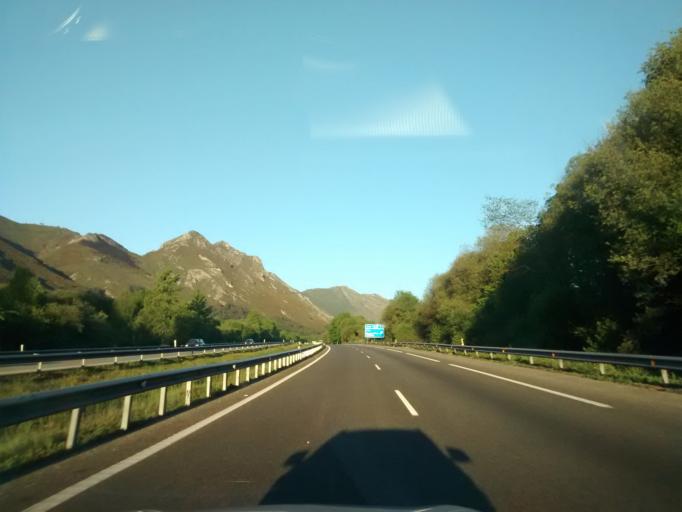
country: ES
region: Asturias
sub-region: Province of Asturias
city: Ribadesella
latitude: 43.4432
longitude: -4.9437
